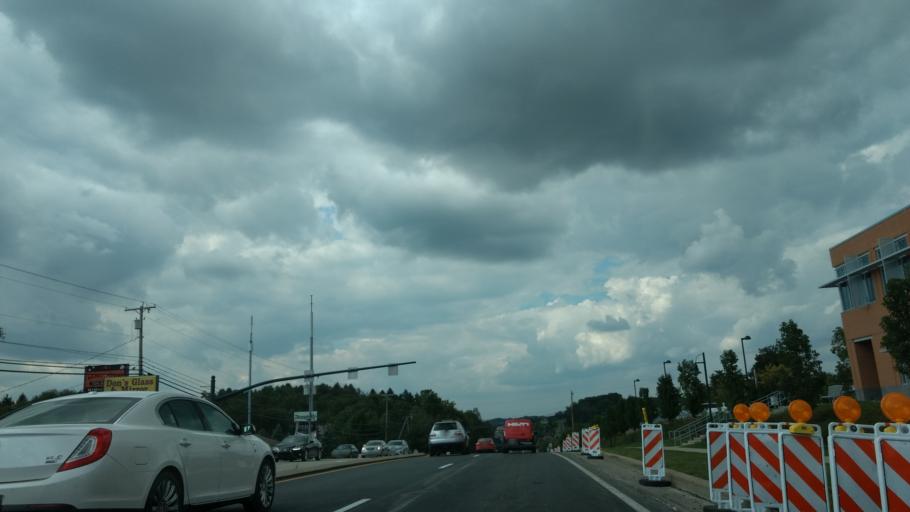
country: US
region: Pennsylvania
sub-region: Allegheny County
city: Bradford Woods
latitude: 40.6382
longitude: -80.0636
